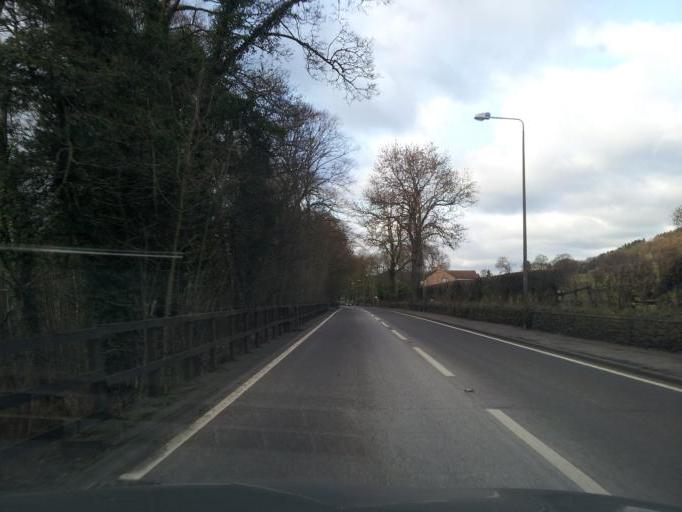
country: GB
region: England
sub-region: Derbyshire
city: Bakewell
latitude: 53.1842
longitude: -1.6110
